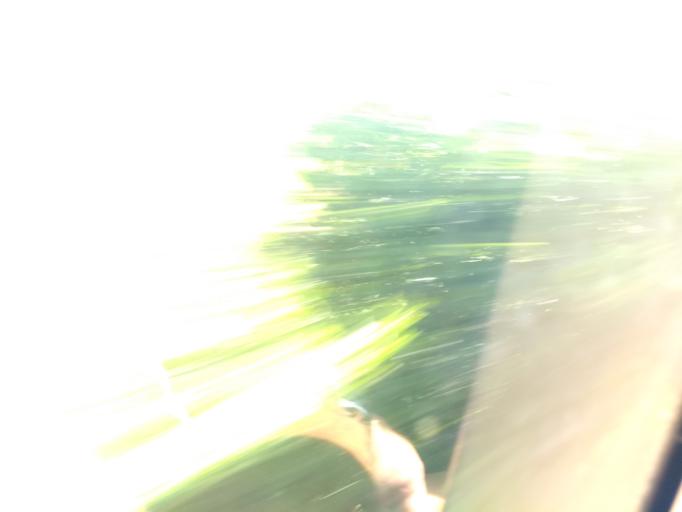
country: GB
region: England
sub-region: Isle of Wight
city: Brading
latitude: 50.6881
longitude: -1.1437
